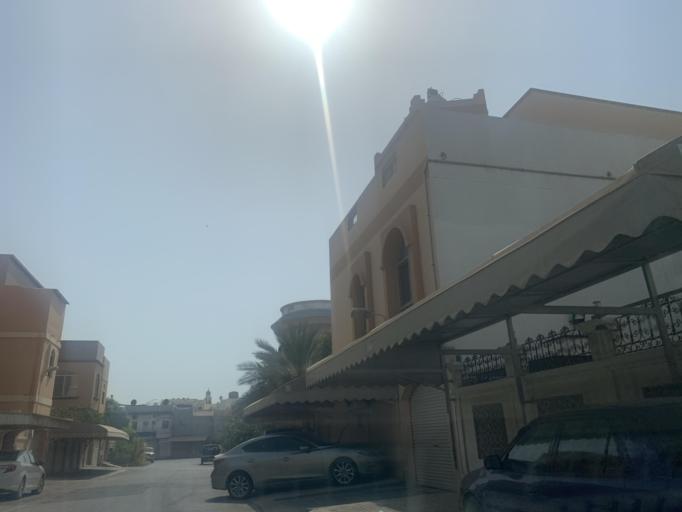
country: BH
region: Manama
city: Jidd Hafs
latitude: 26.2138
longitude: 50.4664
